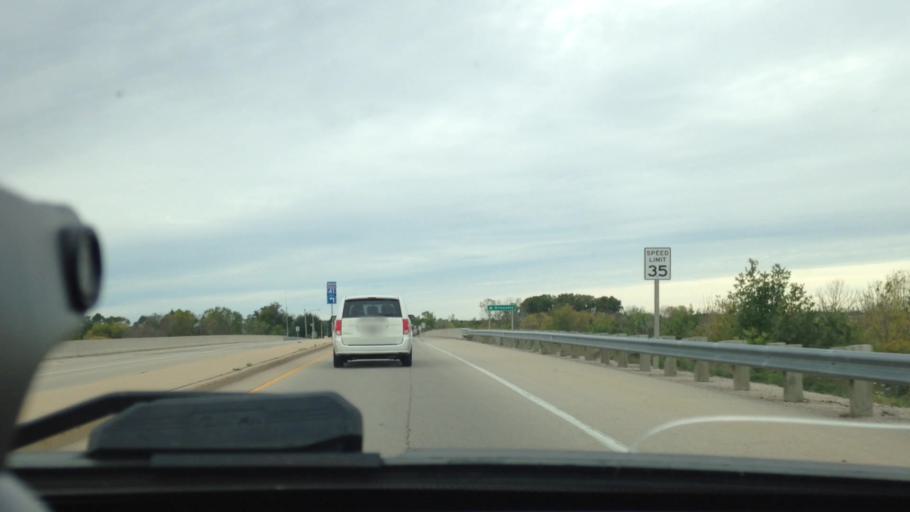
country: US
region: Wisconsin
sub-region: Fond du Lac County
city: North Fond du Lac
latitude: 43.8066
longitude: -88.4984
